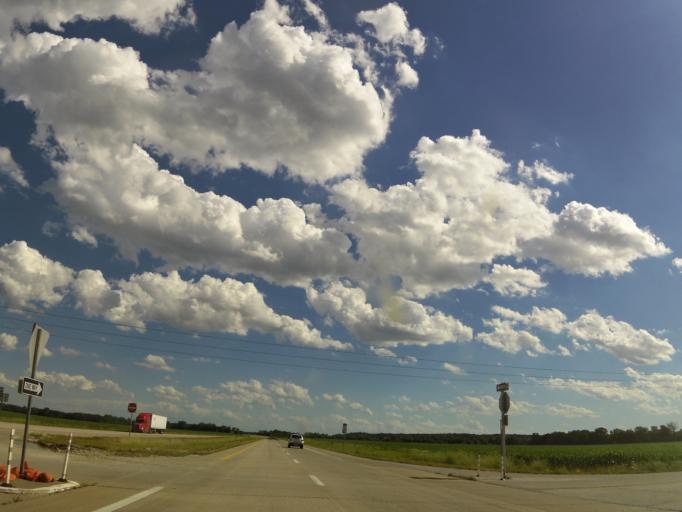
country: US
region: Missouri
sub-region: Clark County
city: Kahoka
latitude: 40.4306
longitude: -91.5704
